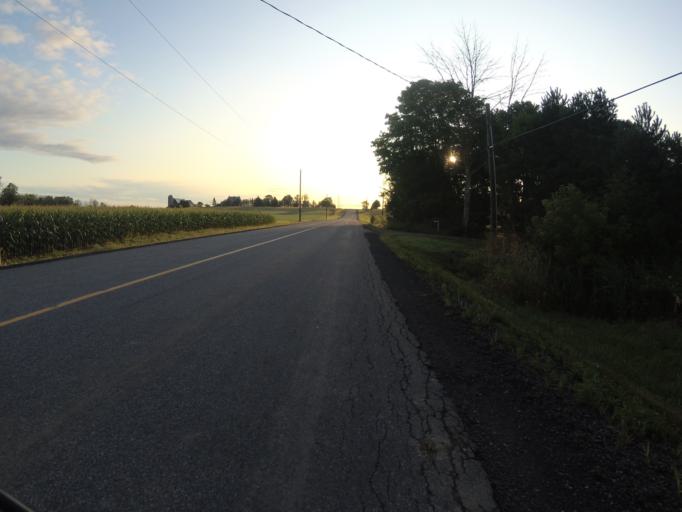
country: CA
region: Ontario
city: Ottawa
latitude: 45.1389
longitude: -75.4595
